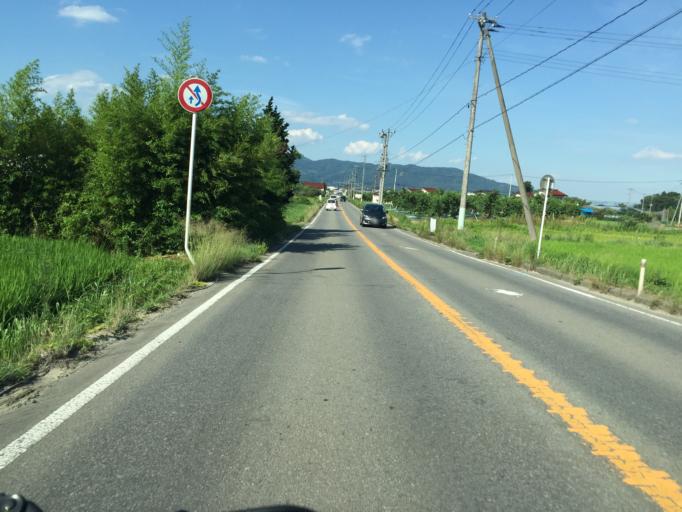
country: JP
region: Fukushima
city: Fukushima-shi
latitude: 37.8145
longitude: 140.4308
